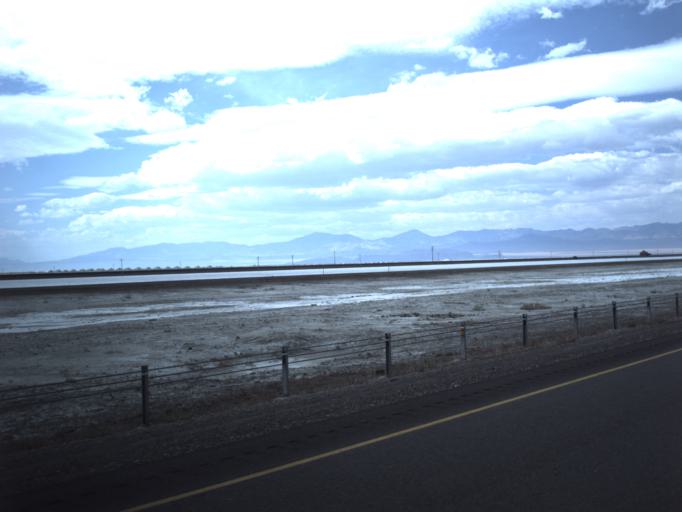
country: US
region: Utah
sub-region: Tooele County
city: Wendover
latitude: 40.7401
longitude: -113.8859
